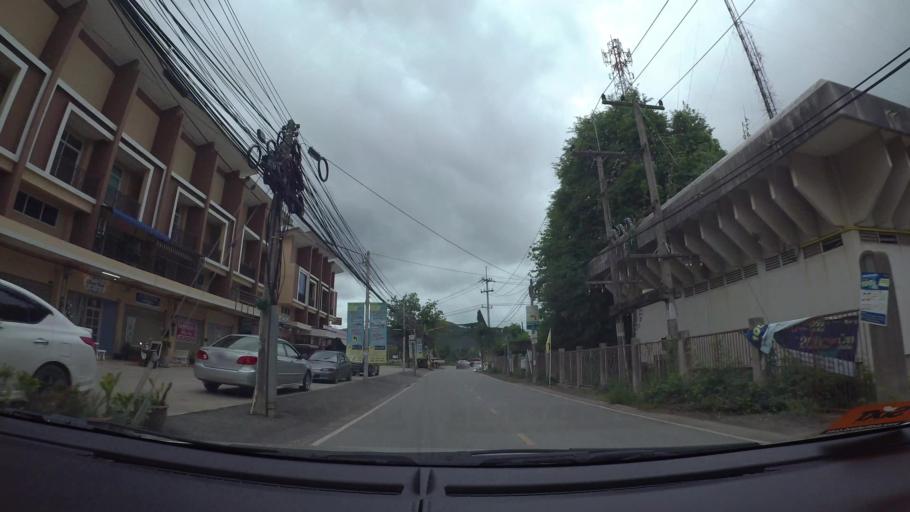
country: TH
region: Chon Buri
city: Sattahip
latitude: 12.7277
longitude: 100.8936
